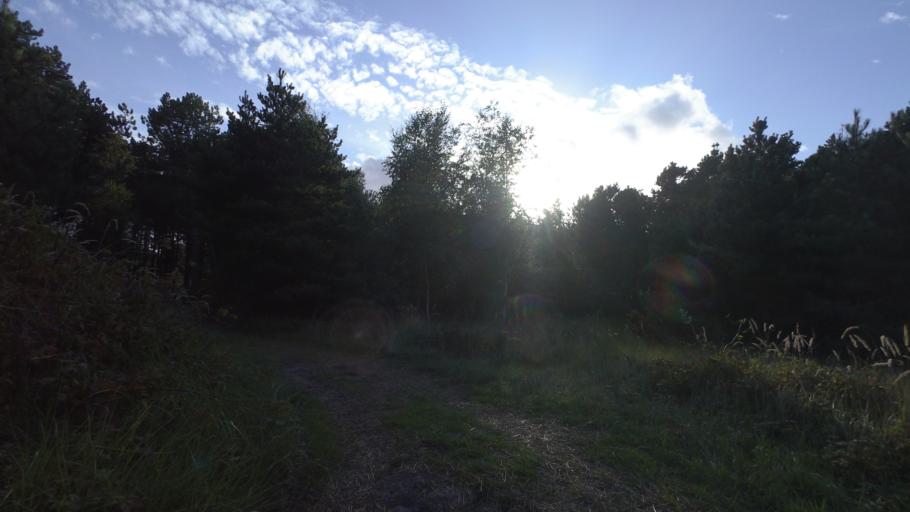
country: NL
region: Friesland
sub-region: Gemeente Ameland
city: Nes
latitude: 53.4591
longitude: 5.8191
